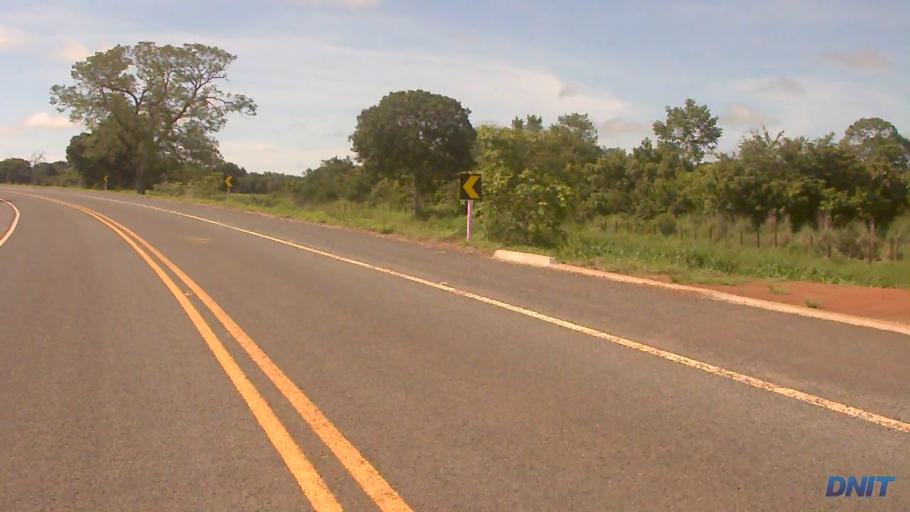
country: BR
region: Goias
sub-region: Sao Miguel Do Araguaia
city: Sao Miguel do Araguaia
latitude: -13.3125
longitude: -50.1709
